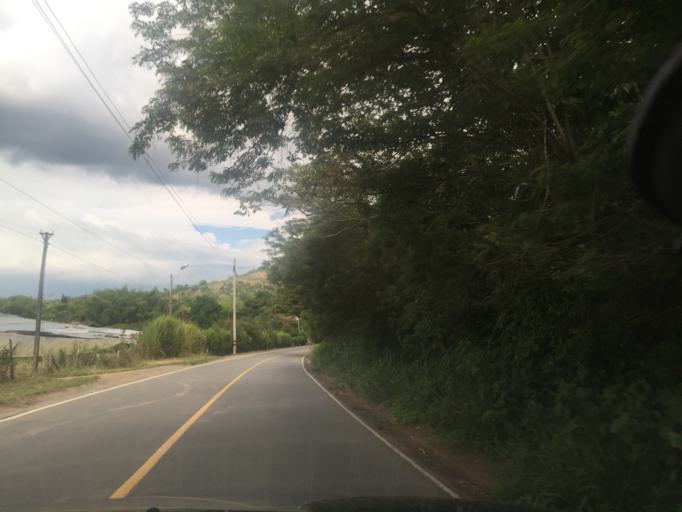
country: CO
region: Valle del Cauca
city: Caicedonia
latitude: 4.3418
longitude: -75.8539
